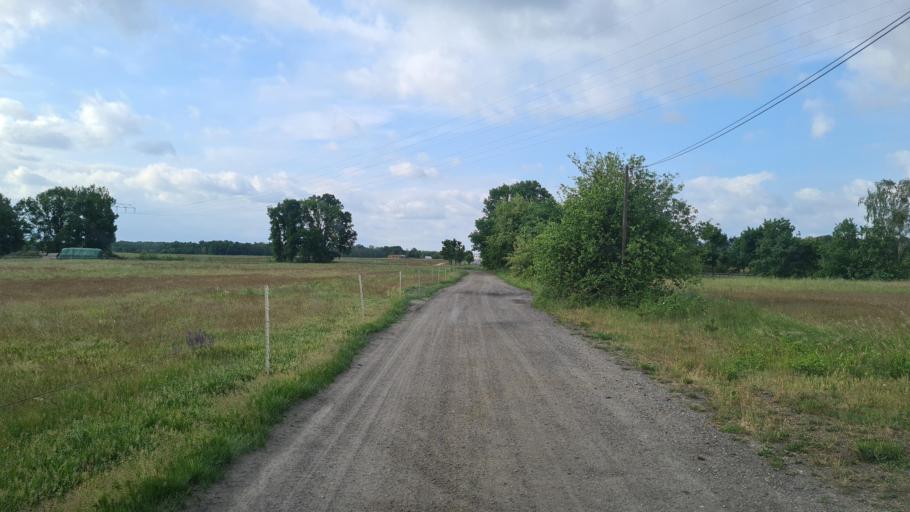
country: DE
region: Brandenburg
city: Grossraschen
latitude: 51.5863
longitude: 14.0322
